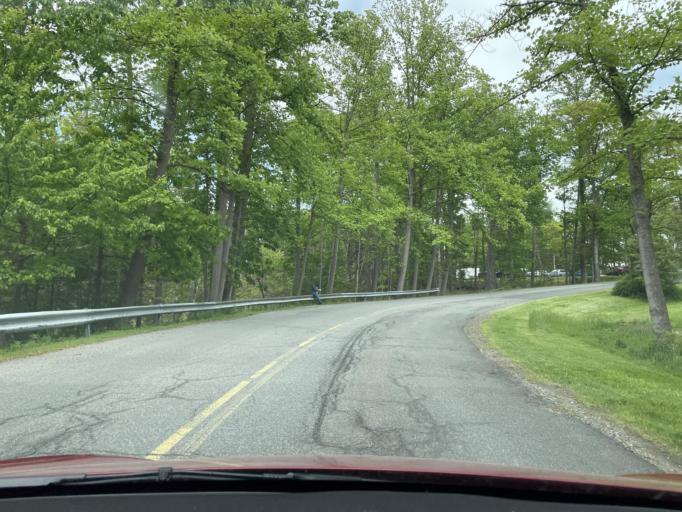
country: US
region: New York
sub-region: Ulster County
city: Woodstock
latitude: 42.0264
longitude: -74.1019
